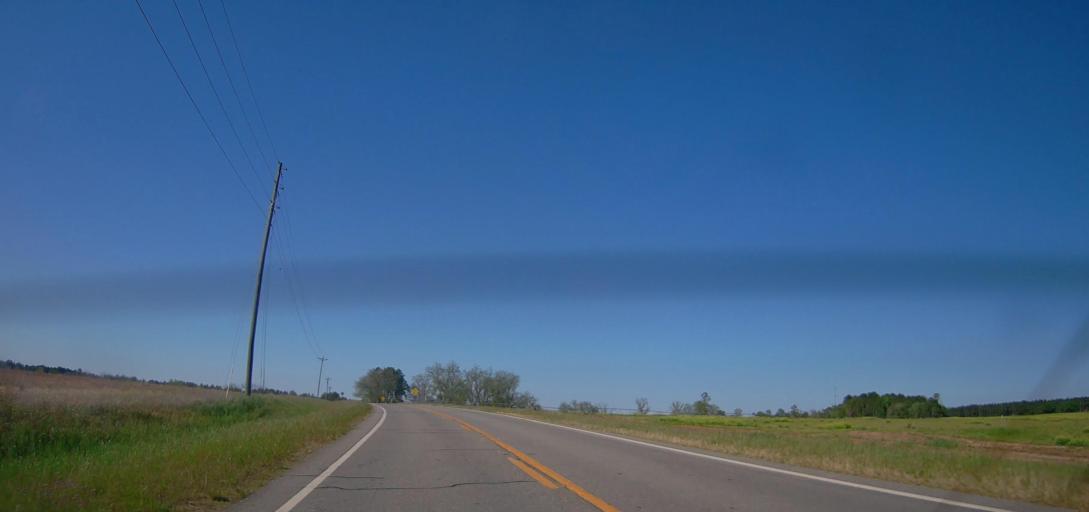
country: US
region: Georgia
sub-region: Wilcox County
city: Rochelle
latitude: 31.9217
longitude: -83.4661
